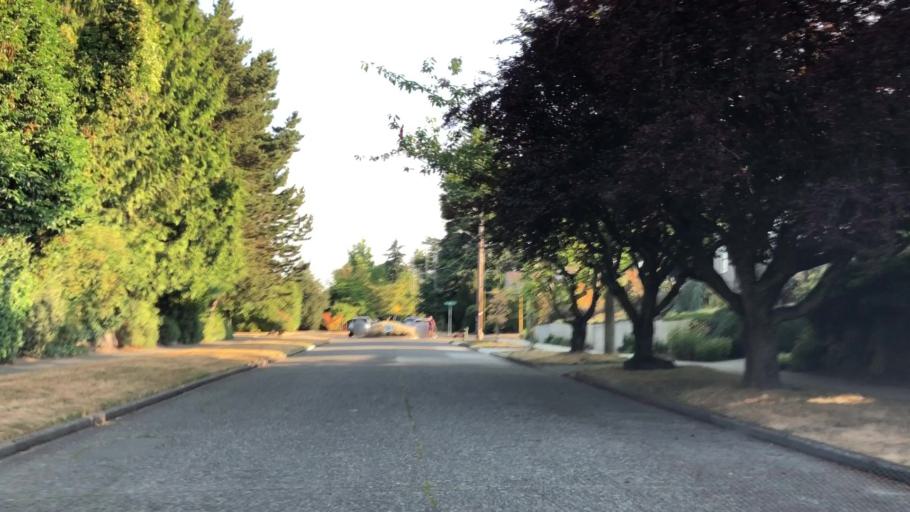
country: US
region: Washington
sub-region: King County
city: Yarrow Point
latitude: 47.6625
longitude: -122.2794
